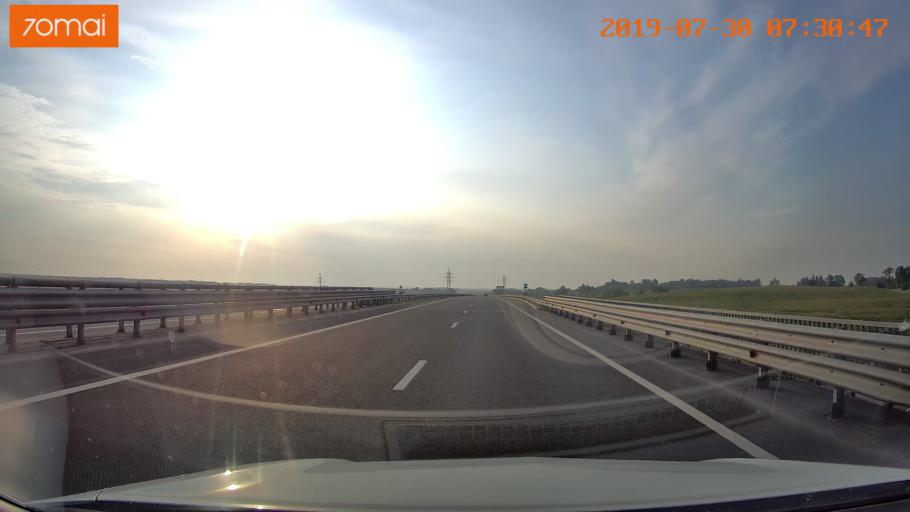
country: RU
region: Kaliningrad
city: Gvardeysk
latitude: 54.6698
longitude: 20.9737
